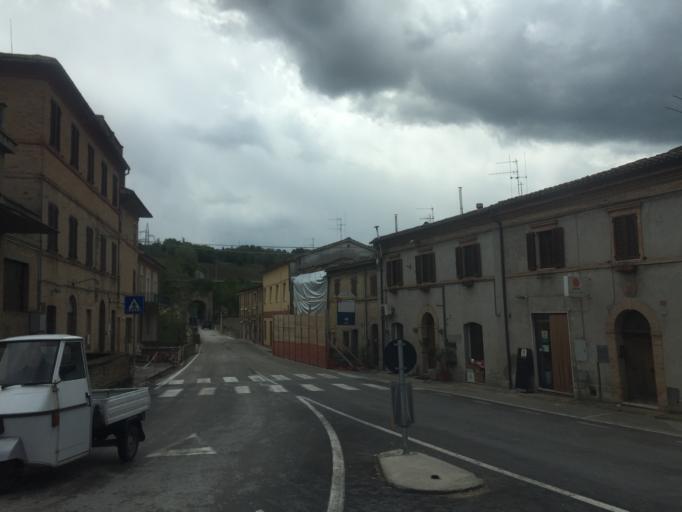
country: IT
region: The Marches
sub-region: Provincia di Macerata
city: Tolentino
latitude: 43.2066
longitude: 13.2860
